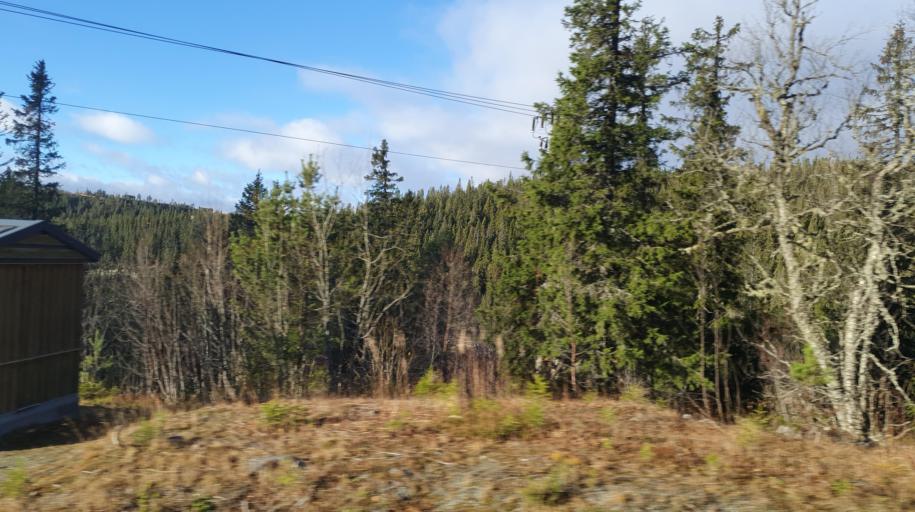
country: NO
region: Buskerud
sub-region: Krodsherad
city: Noresund
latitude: 60.2196
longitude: 9.5338
